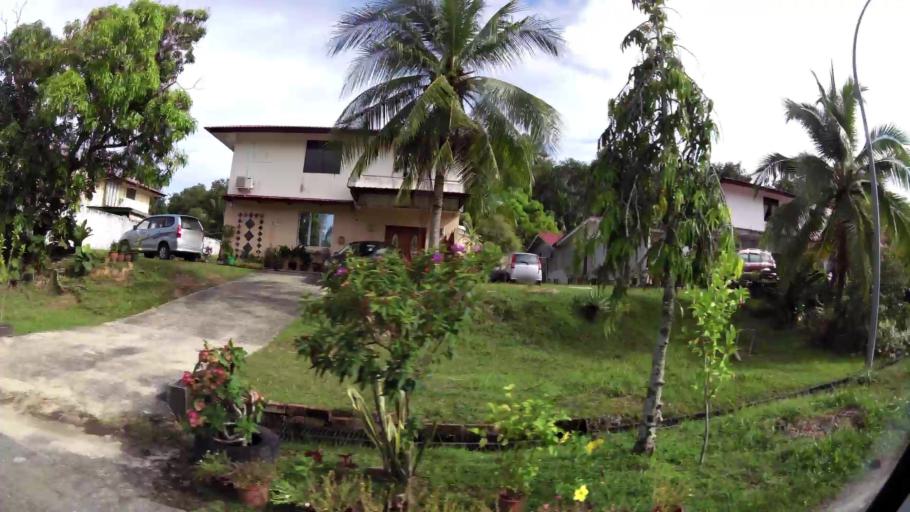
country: BN
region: Brunei and Muara
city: Bandar Seri Begawan
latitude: 4.8946
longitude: 114.8858
